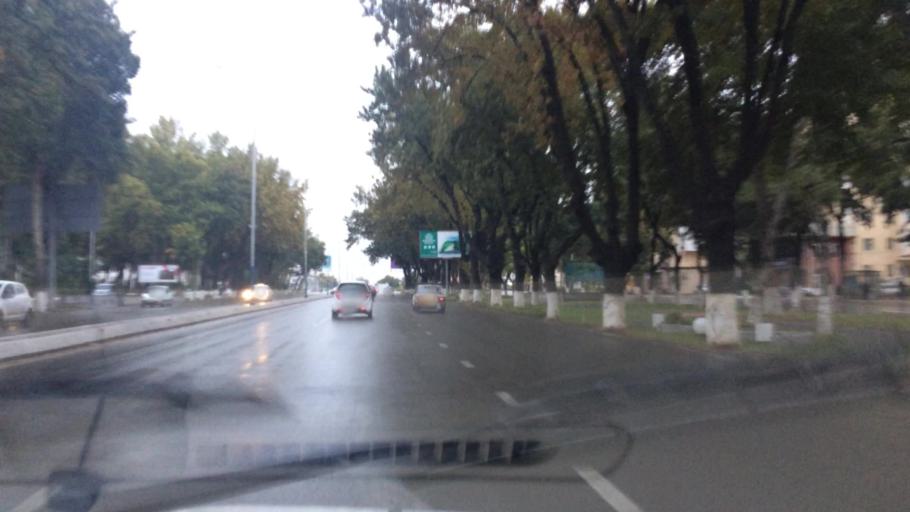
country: UZ
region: Toshkent Shahri
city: Tashkent
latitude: 41.2963
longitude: 69.2280
